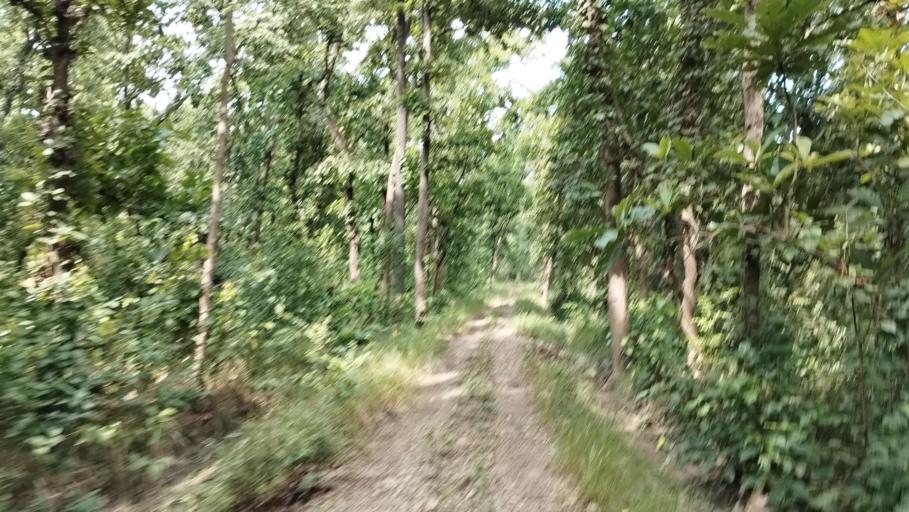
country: NP
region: Far Western
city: Tikapur
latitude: 28.5089
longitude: 81.2682
